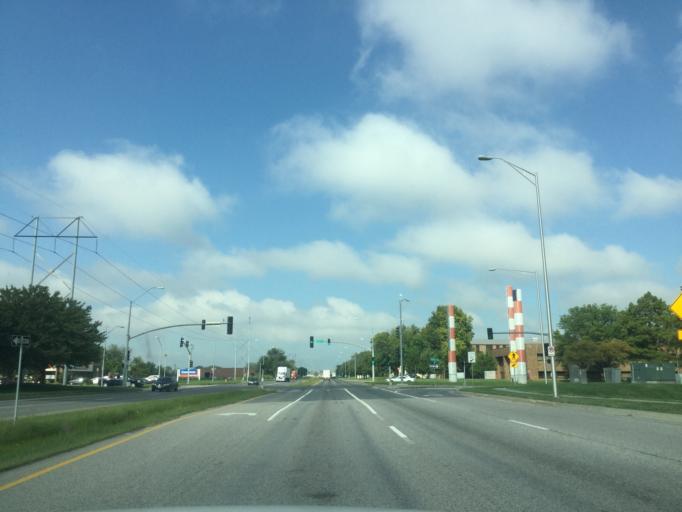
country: US
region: Missouri
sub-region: Clay County
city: North Kansas City
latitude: 39.1303
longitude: -94.5051
